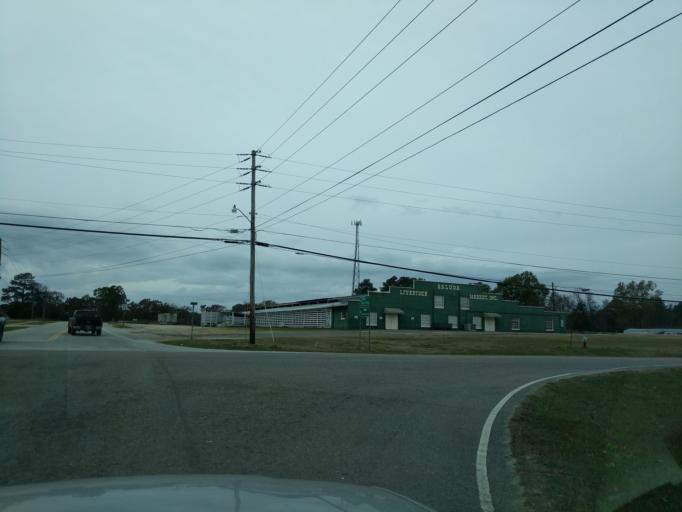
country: US
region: South Carolina
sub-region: Saluda County
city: Saluda
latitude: 34.0145
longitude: -81.7683
